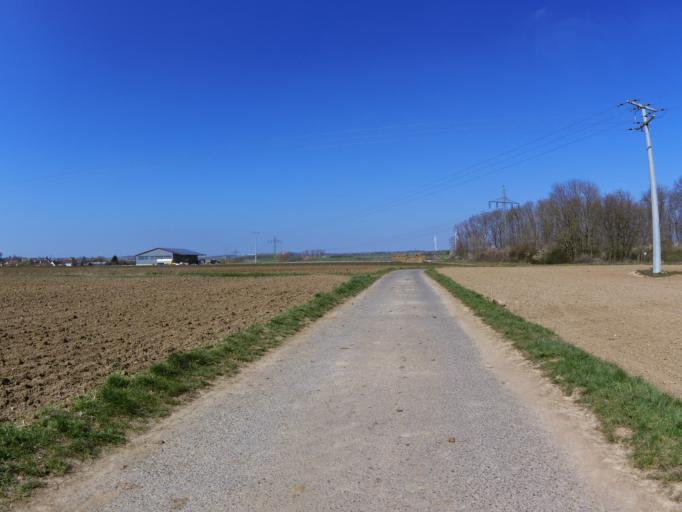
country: DE
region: Bavaria
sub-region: Regierungsbezirk Unterfranken
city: Sulzfeld am Main
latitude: 49.7275
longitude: 10.0978
